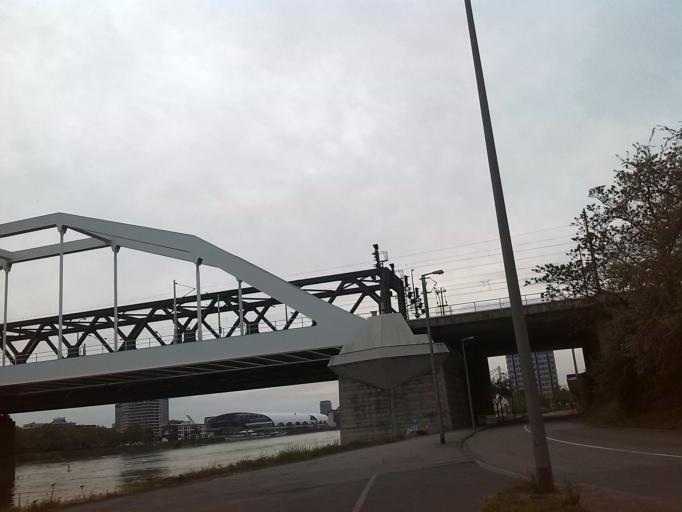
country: DE
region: Rheinland-Pfalz
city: Ludwigshafen am Rhein
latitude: 49.4811
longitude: 8.4588
